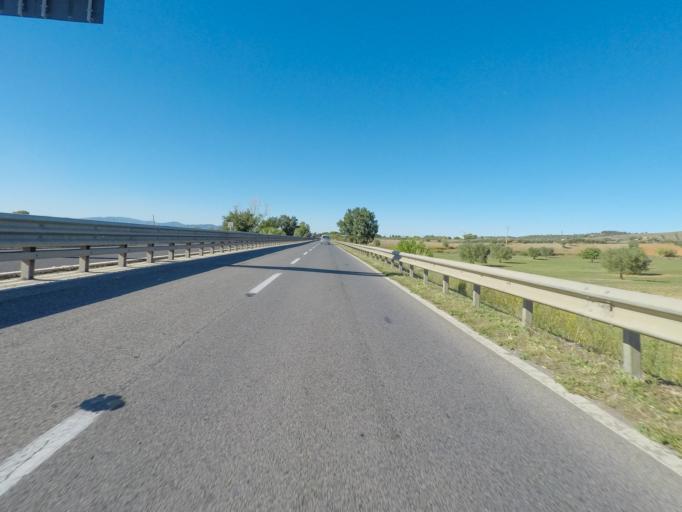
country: IT
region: Tuscany
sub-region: Provincia di Grosseto
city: Grosseto
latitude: 42.7178
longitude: 11.1418
